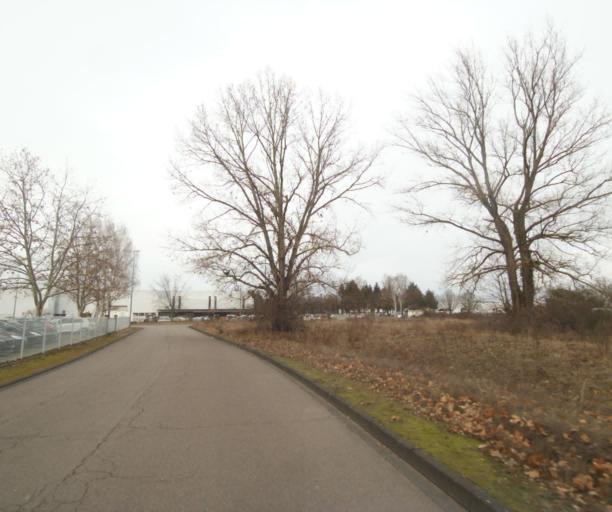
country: FR
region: Rhone-Alpes
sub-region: Departement de la Loire
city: Roanne
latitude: 46.0590
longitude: 4.0809
